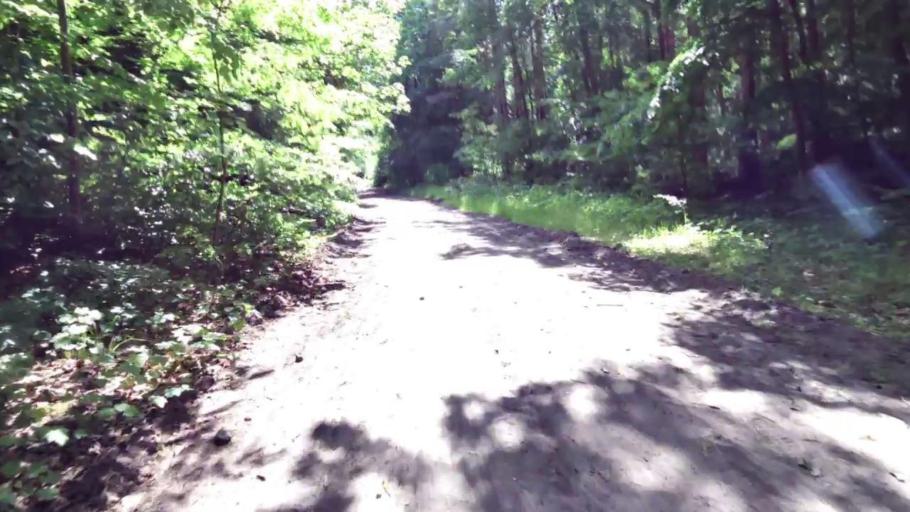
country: PL
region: West Pomeranian Voivodeship
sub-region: Powiat kamienski
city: Miedzyzdroje
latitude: 53.9321
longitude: 14.5321
